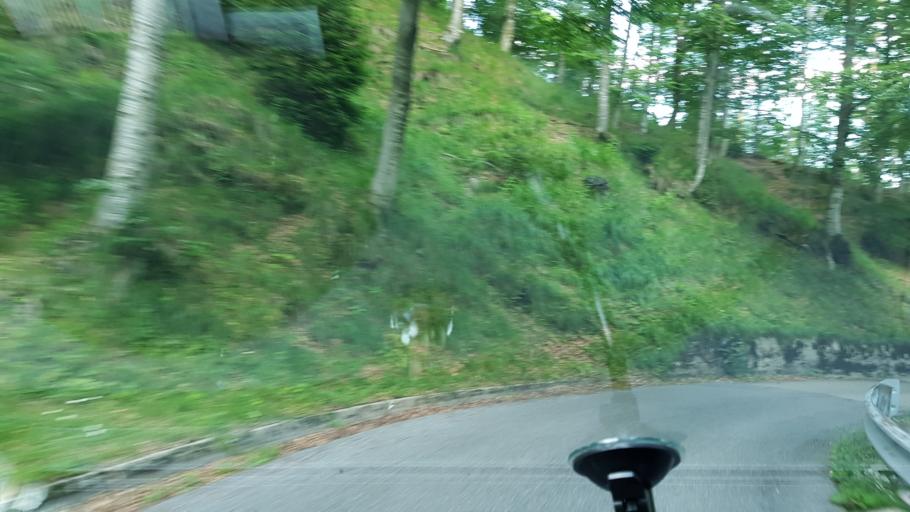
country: IT
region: Friuli Venezia Giulia
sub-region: Provincia di Udine
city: Prato
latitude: 46.3315
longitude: 13.3432
